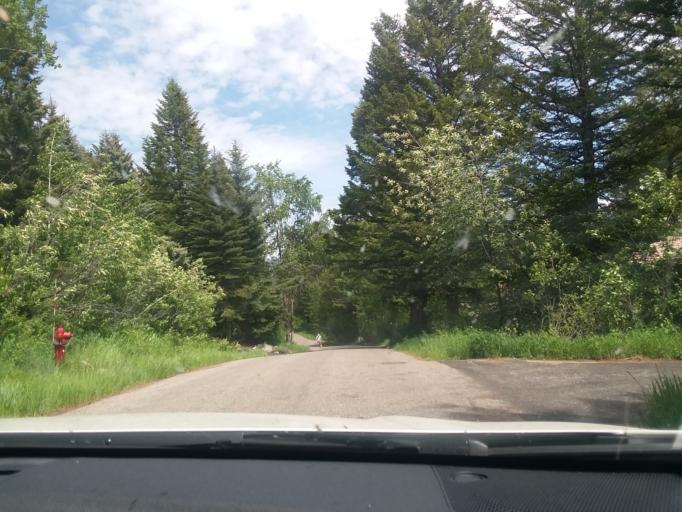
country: US
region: Wyoming
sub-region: Teton County
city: Moose Wilson Road
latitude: 43.5869
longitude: -110.8385
